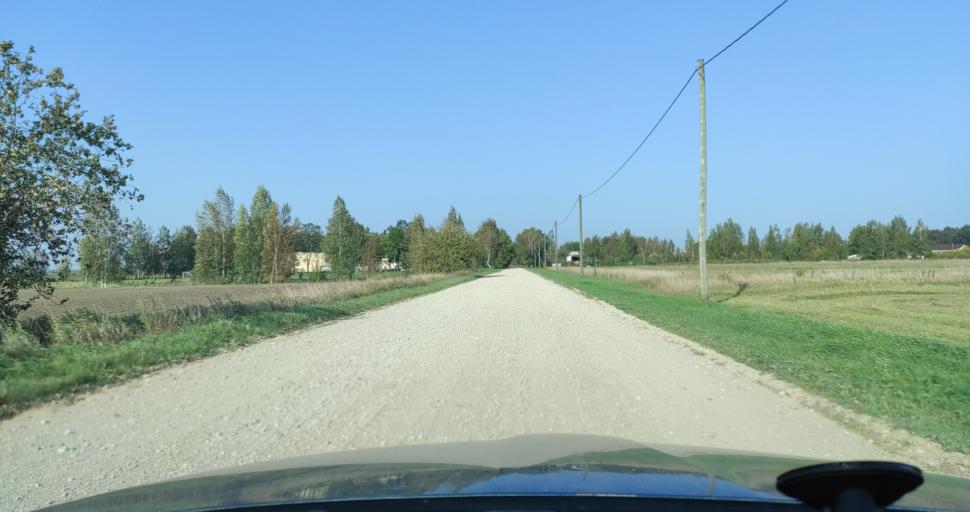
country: LV
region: Ventspils Rajons
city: Piltene
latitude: 57.2233
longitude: 21.6126
